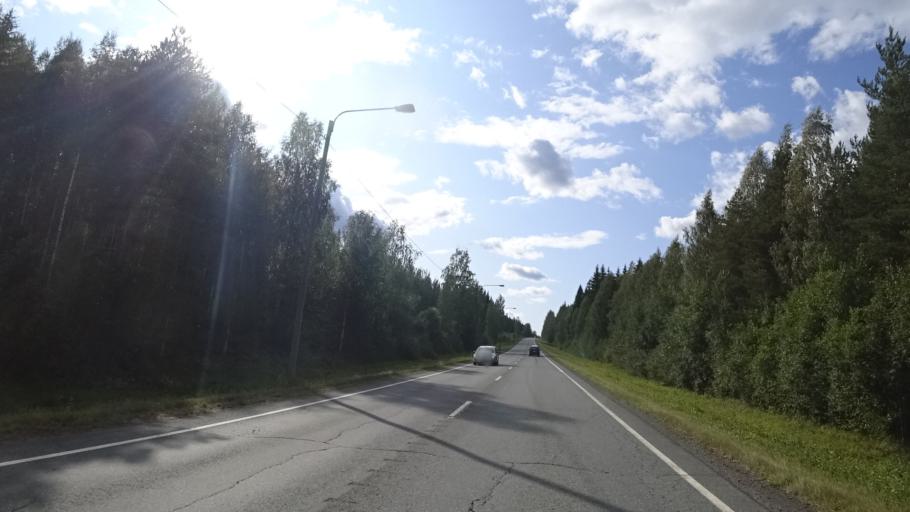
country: FI
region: North Karelia
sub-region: Keski-Karjala
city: Tohmajaervi
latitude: 62.2216
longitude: 30.3755
